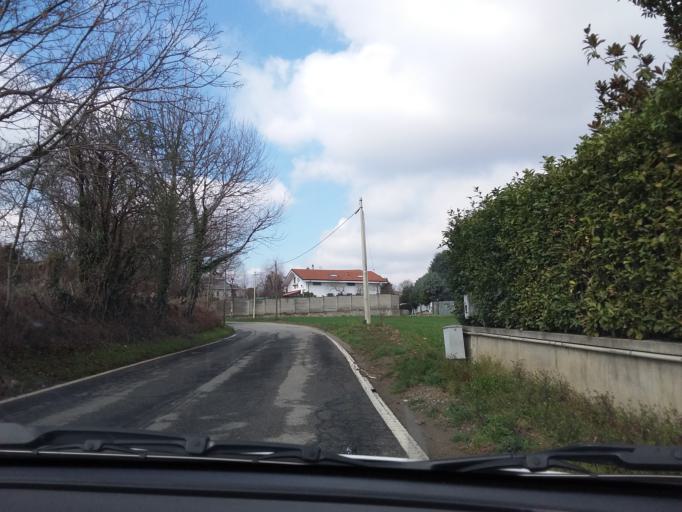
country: IT
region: Piedmont
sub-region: Provincia di Torino
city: Tetti Neirotti
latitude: 45.0557
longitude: 7.5334
